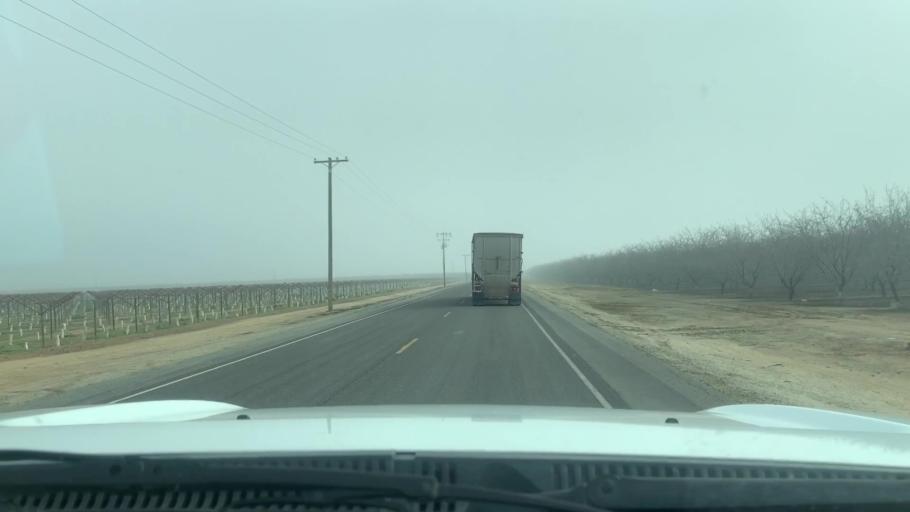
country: US
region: California
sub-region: Kern County
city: Buttonwillow
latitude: 35.5005
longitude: -119.4257
